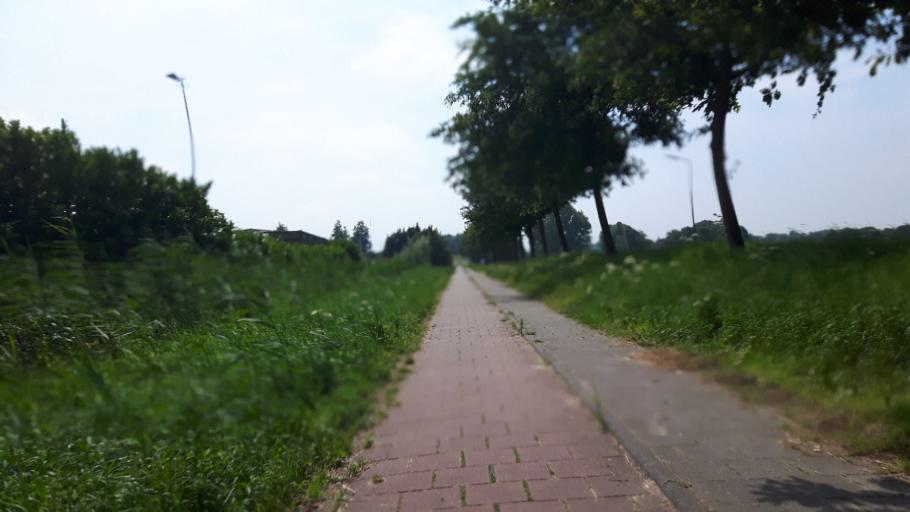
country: NL
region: Utrecht
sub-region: Gemeente Lopik
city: Lopik
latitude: 51.9690
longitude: 4.9522
